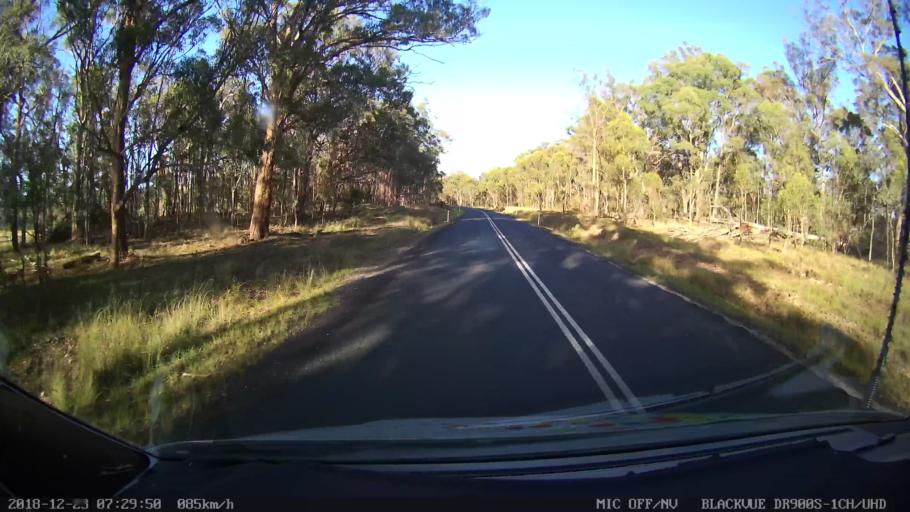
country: AU
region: New South Wales
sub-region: Armidale Dumaresq
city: Enmore
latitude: -30.4981
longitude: 152.1514
